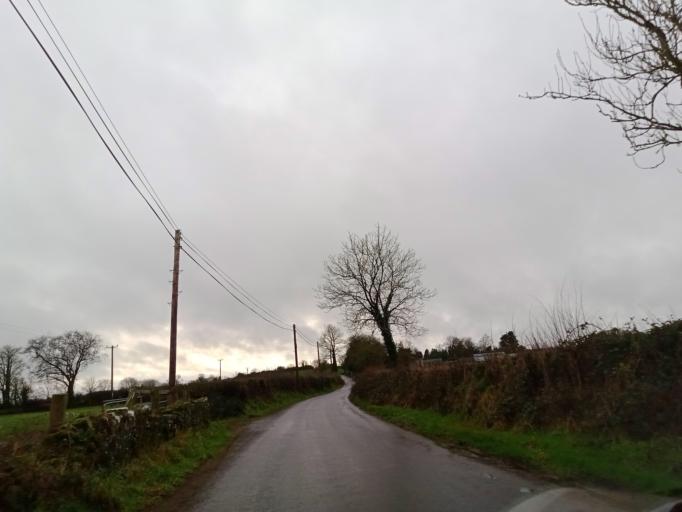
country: IE
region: Munster
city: Fethard
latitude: 52.5599
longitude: -7.6941
